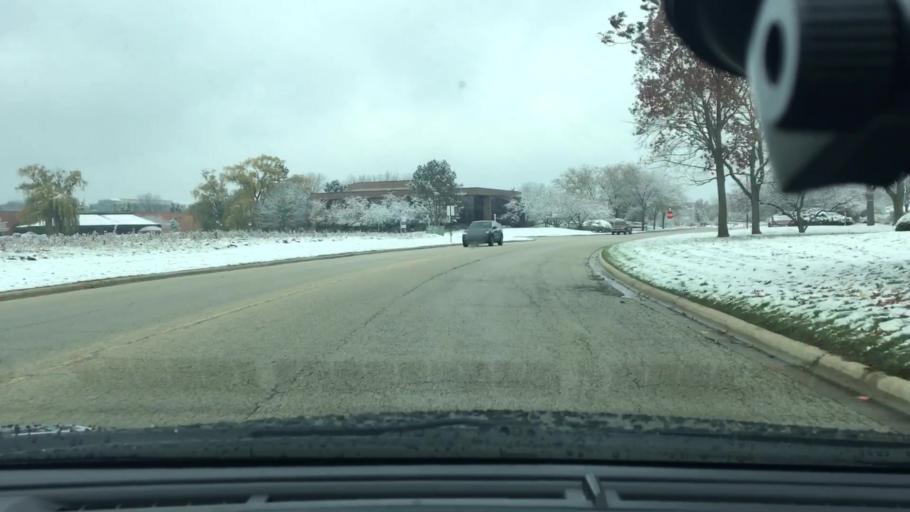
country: US
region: Illinois
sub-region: Lake County
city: Lincolnshire
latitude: 42.1914
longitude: -87.9367
